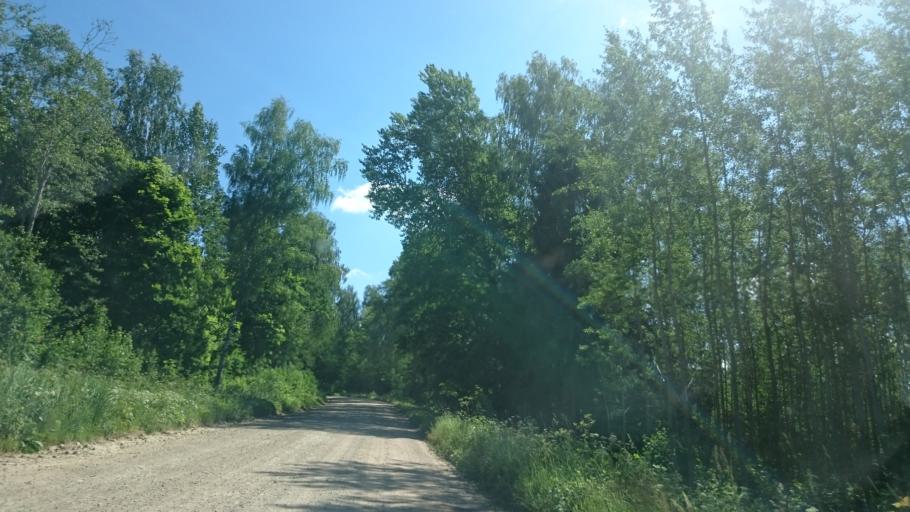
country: LV
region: Cibla
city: Cibla
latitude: 56.5393
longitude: 27.9213
